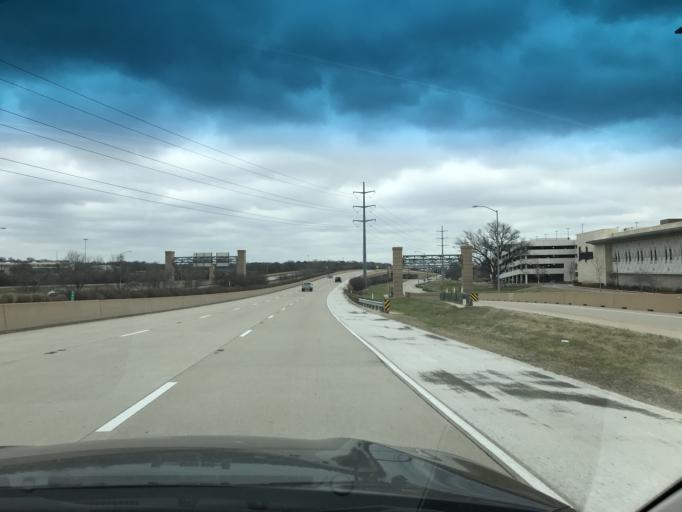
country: US
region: Texas
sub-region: Tarrant County
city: Westworth
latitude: 32.7101
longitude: -97.4021
